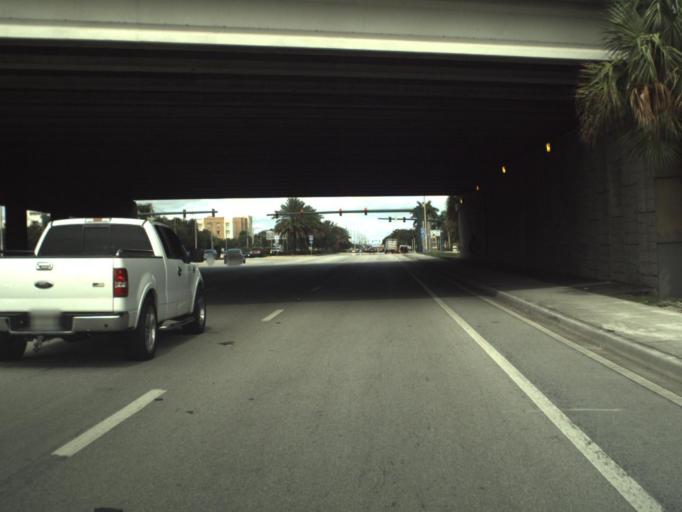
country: US
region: Florida
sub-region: Palm Beach County
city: Mangonia Park
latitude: 26.7592
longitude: -80.0908
